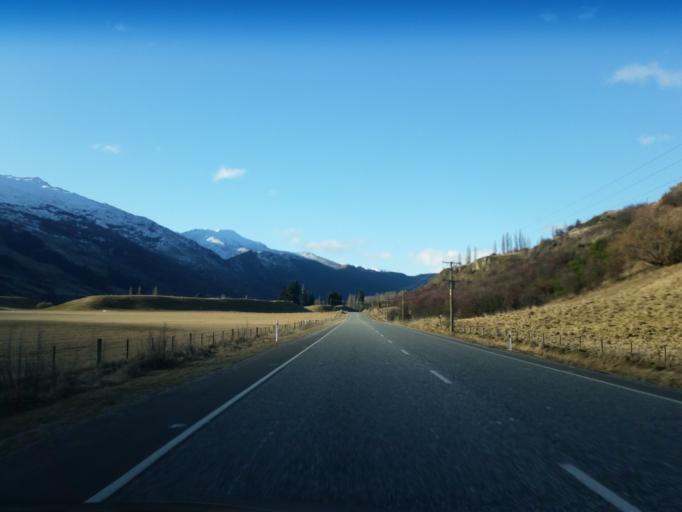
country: NZ
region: Otago
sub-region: Queenstown-Lakes District
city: Queenstown
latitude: -44.9653
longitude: 168.7127
